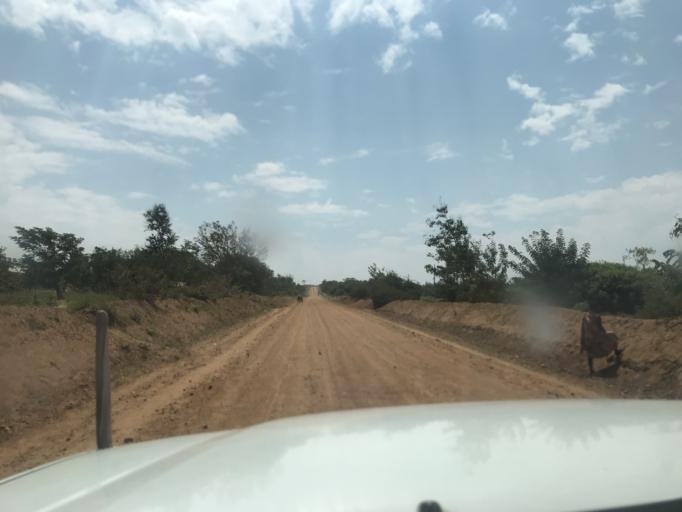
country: TZ
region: Mara
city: Nyamuswa
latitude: -1.9486
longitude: 33.9880
